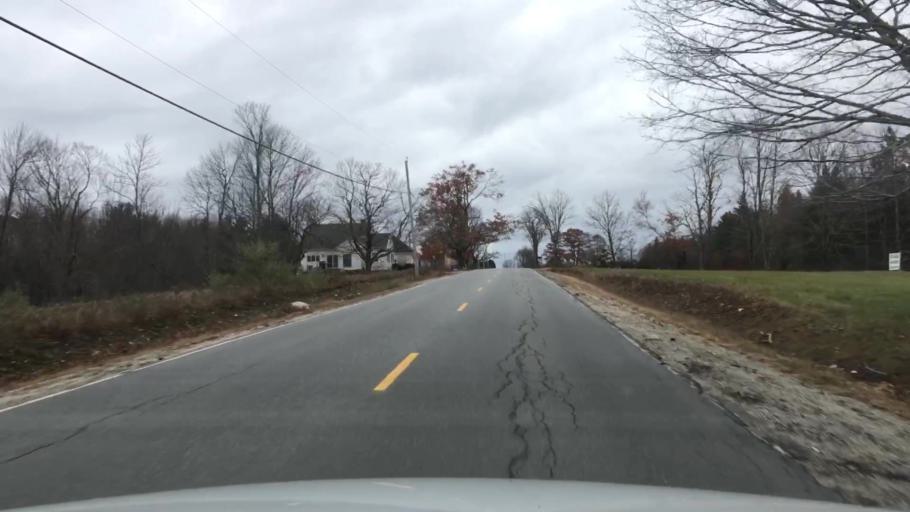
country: US
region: Maine
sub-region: Hancock County
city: Penobscot
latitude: 44.4368
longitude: -68.6327
